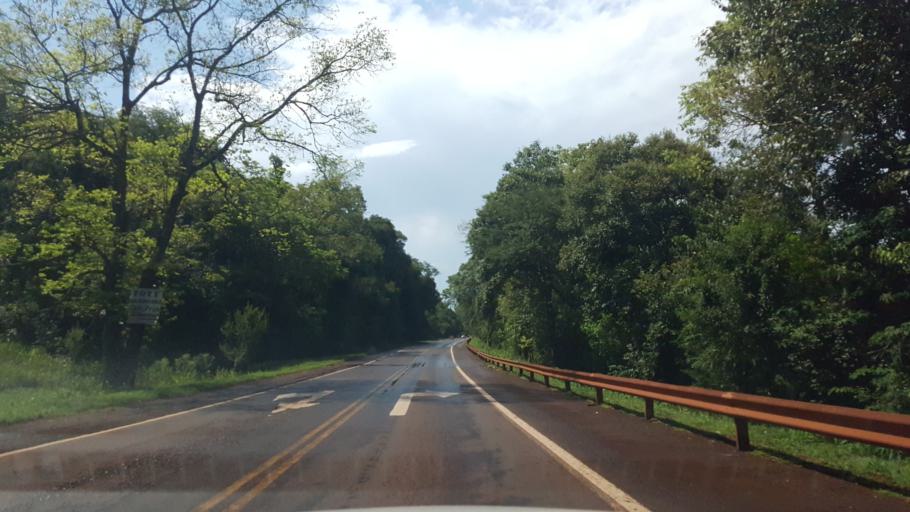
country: AR
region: Misiones
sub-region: Departamento de Eldorado
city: Eldorado
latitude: -26.3592
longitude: -54.6197
